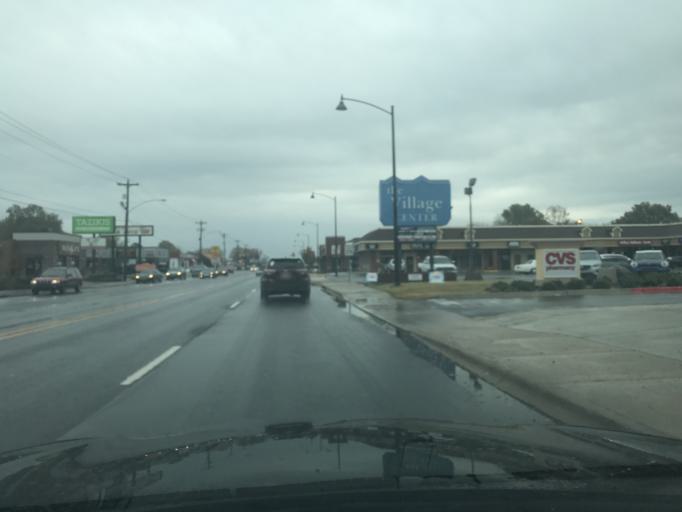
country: US
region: Arkansas
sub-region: Faulkner County
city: Conway
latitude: 35.0917
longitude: -92.4361
